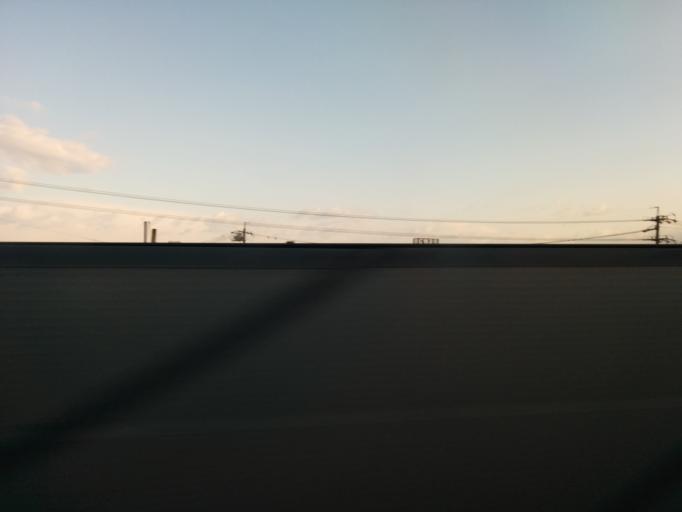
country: JP
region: Aichi
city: Inazawa
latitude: 35.2256
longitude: 136.8185
